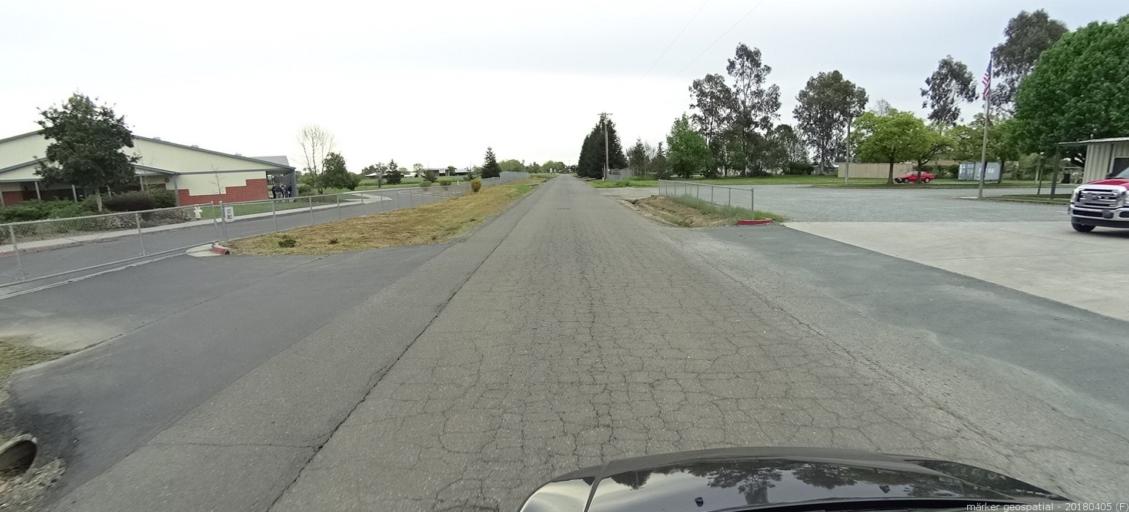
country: US
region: California
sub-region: Sacramento County
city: Herald
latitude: 38.2941
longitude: -121.2406
